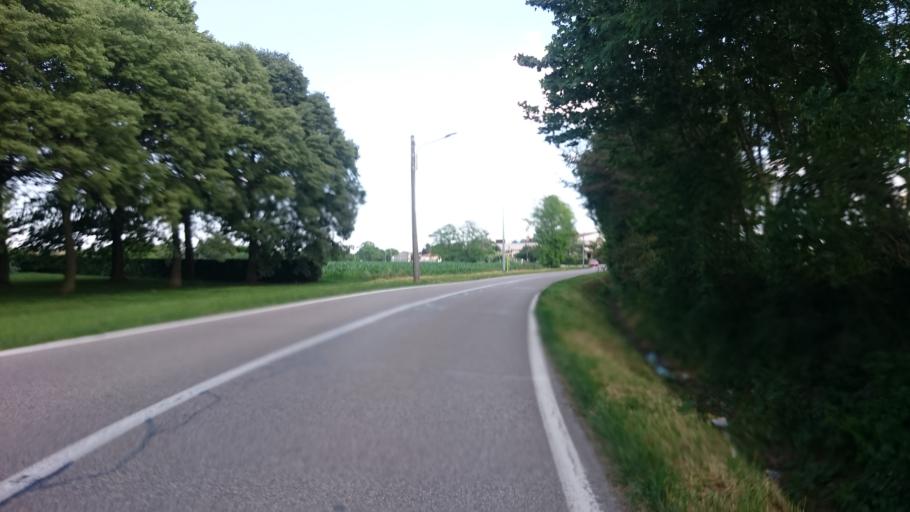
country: IT
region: Lombardy
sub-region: Provincia di Mantova
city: Lunetta-Frassino
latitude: 45.1551
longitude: 10.8257
